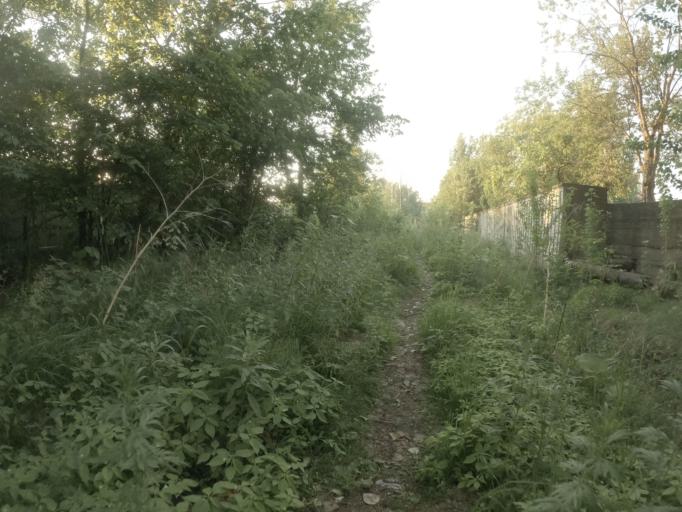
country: RU
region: St.-Petersburg
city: Krasnogvargeisky
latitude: 59.9455
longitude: 30.4410
